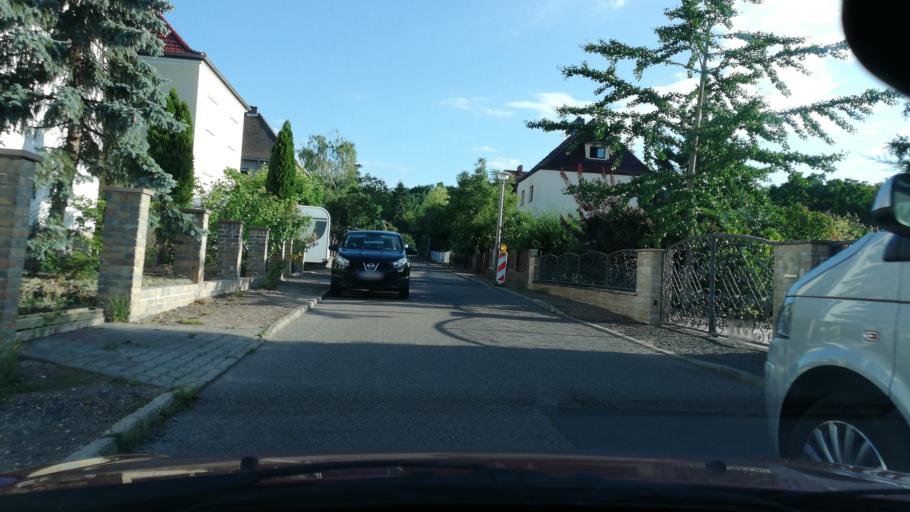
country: DE
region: Saxony-Anhalt
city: Halle Neustadt
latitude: 51.4936
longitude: 11.9096
